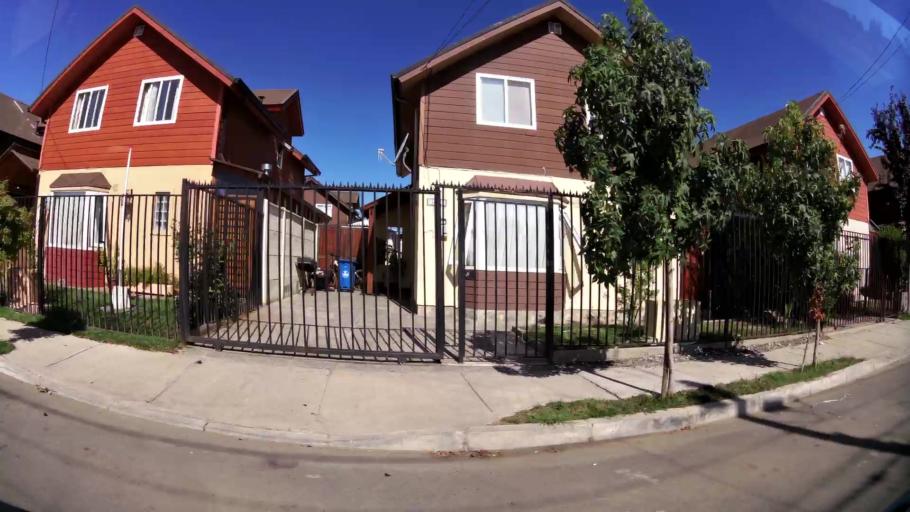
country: CL
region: Maule
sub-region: Provincia de Talca
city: Talca
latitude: -35.4174
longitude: -71.6160
